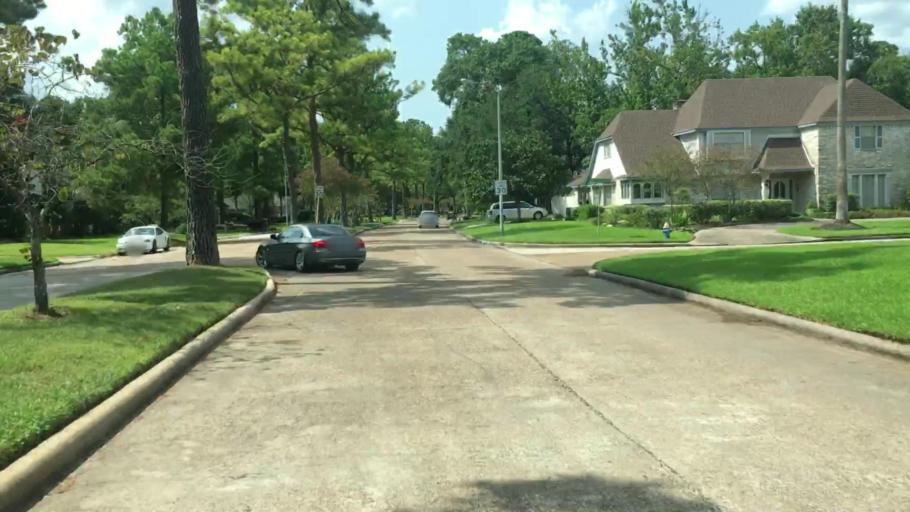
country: US
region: Texas
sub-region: Harris County
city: Atascocita
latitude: 30.0051
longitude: -95.1558
